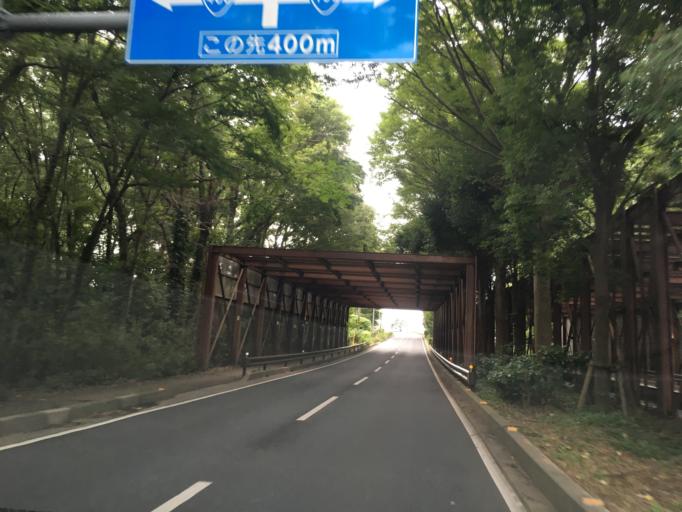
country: JP
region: Saitama
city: Tokorozawa
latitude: 35.8035
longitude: 139.4973
